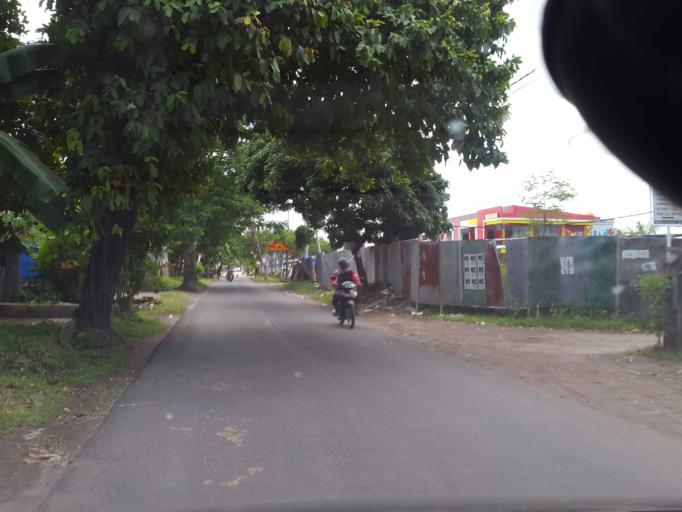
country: ID
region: West Nusa Tenggara
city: Mambalan
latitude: -8.5395
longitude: 116.0849
